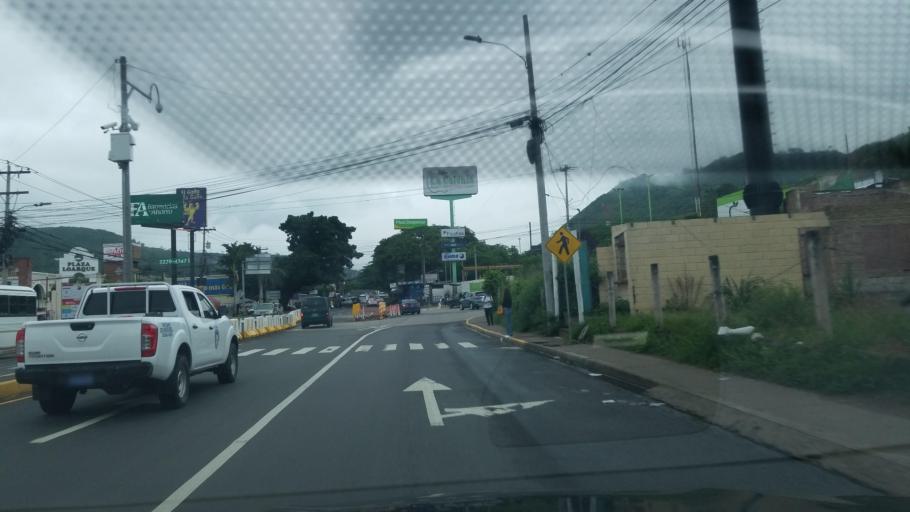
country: HN
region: Francisco Morazan
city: Yaguacire
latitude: 14.0462
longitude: -87.2121
